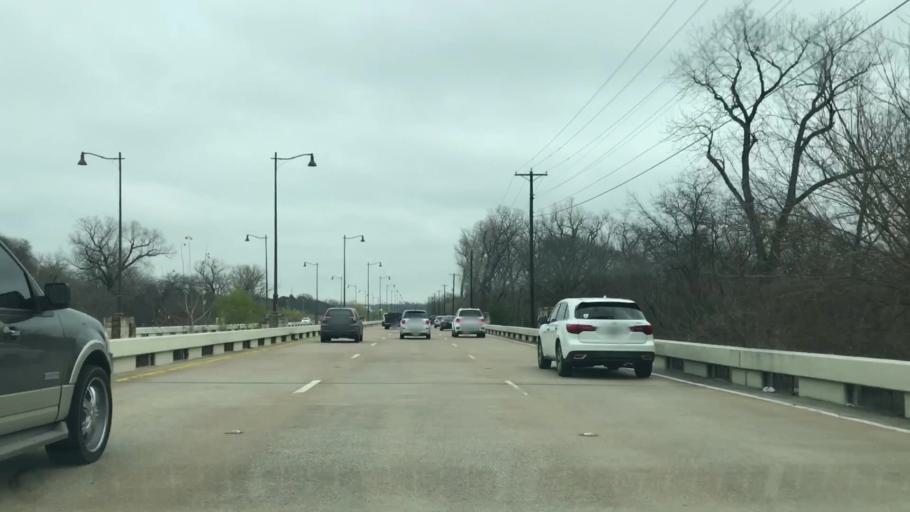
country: US
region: Texas
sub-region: Dallas County
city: Highland Park
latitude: 32.8559
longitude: -96.7284
